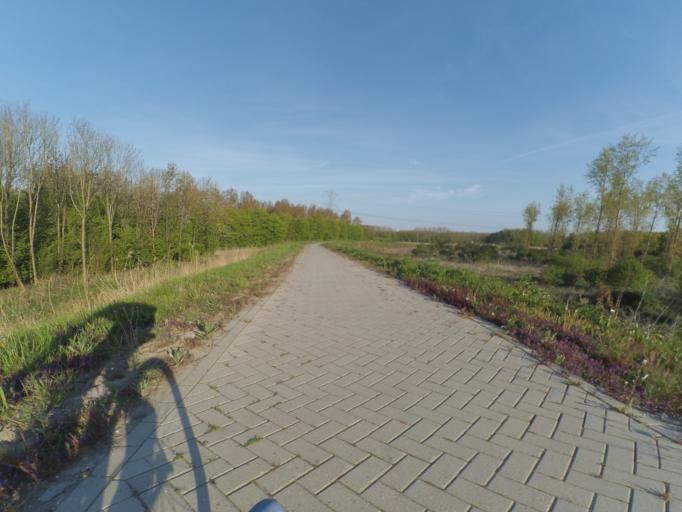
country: NL
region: Flevoland
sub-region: Gemeente Almere
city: Almere Stad
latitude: 52.4055
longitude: 5.3573
